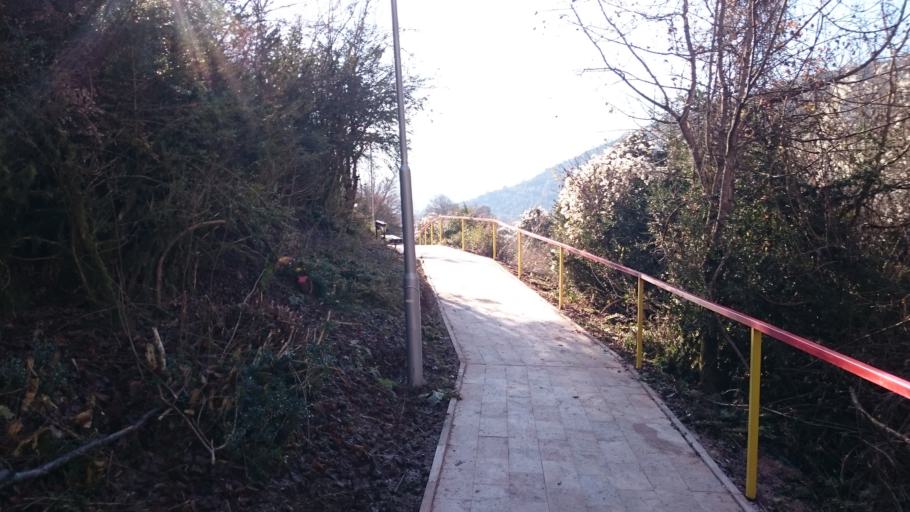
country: MK
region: Makedonski Brod
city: Makedonski Brod
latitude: 41.5473
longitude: 21.2514
